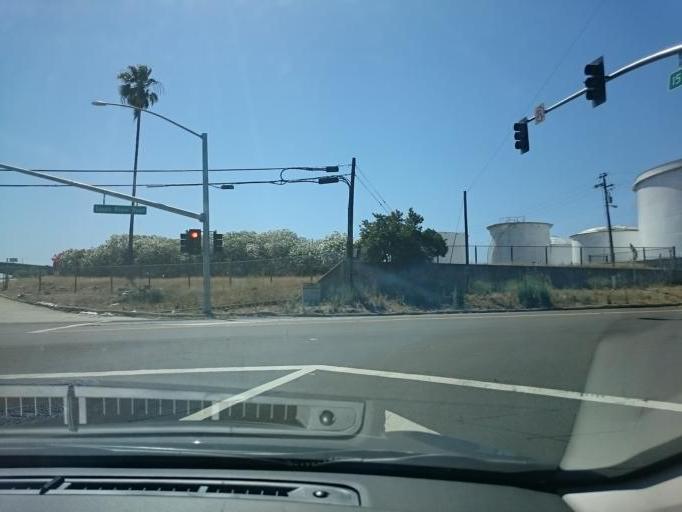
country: US
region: California
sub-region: Yolo County
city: West Sacramento
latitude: 38.5715
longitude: -121.5207
